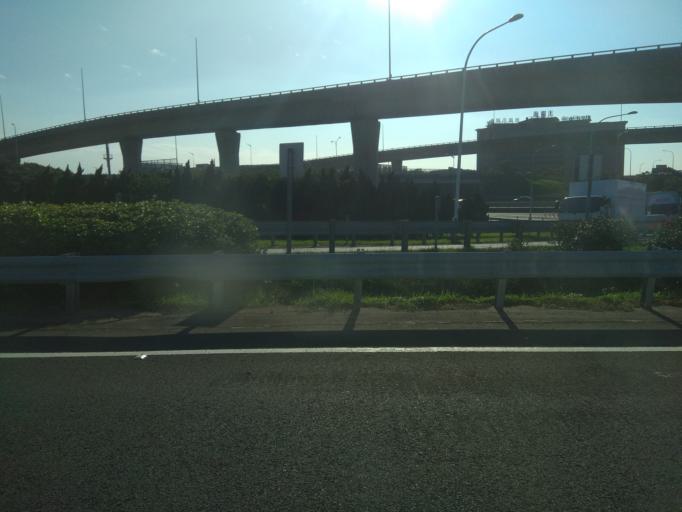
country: TW
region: Taiwan
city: Taoyuan City
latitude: 25.0599
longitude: 121.2142
